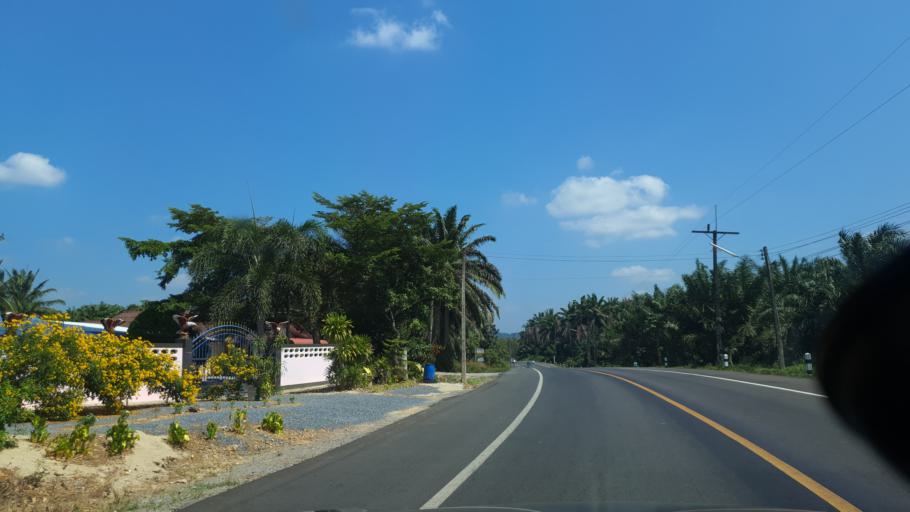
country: TH
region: Krabi
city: Khlong Thom
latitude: 7.9394
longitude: 99.1513
